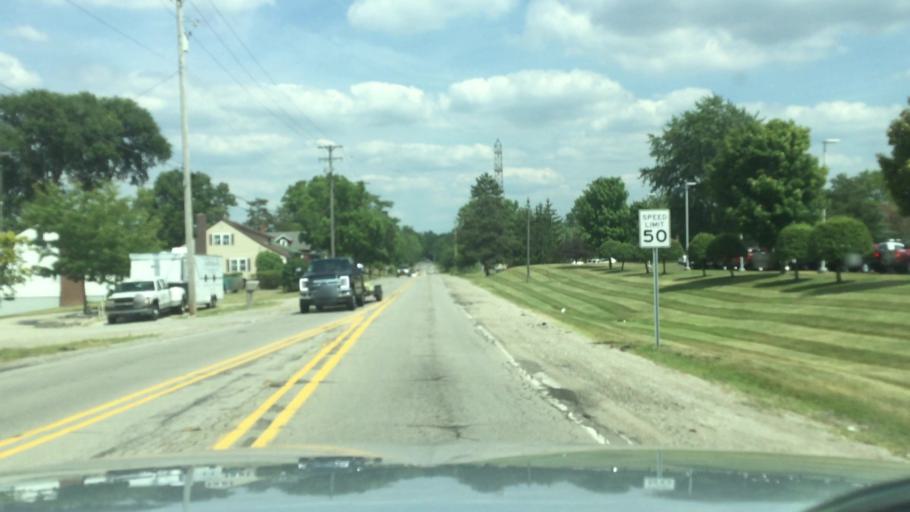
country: US
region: Michigan
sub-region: Genesee County
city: Grand Blanc
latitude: 42.9446
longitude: -83.6495
